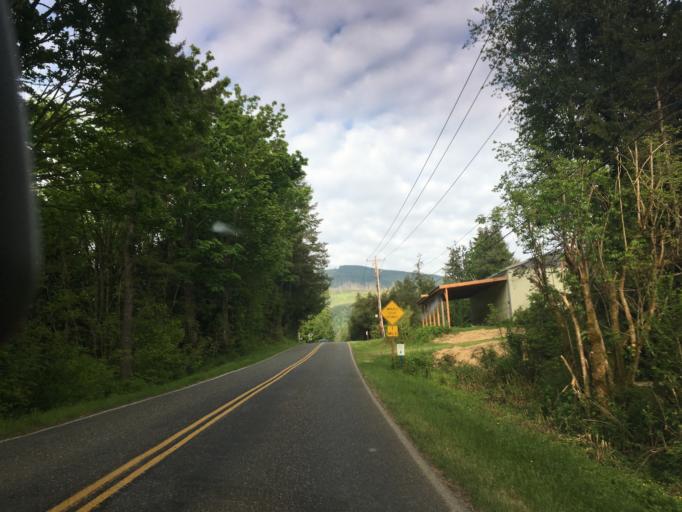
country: US
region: Washington
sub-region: Whatcom County
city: Sudden Valley
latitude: 48.7749
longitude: -122.3541
